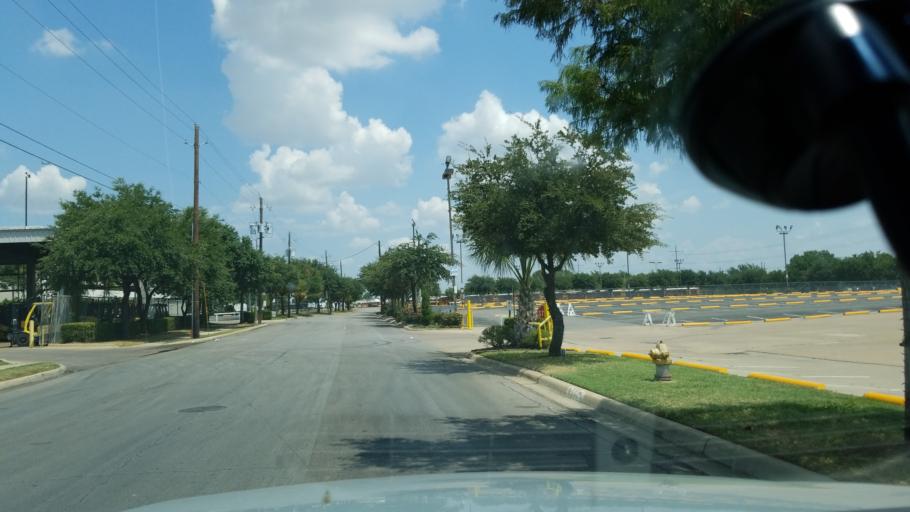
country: US
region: Texas
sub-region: Dallas County
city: Farmers Branch
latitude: 32.8679
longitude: -96.8937
